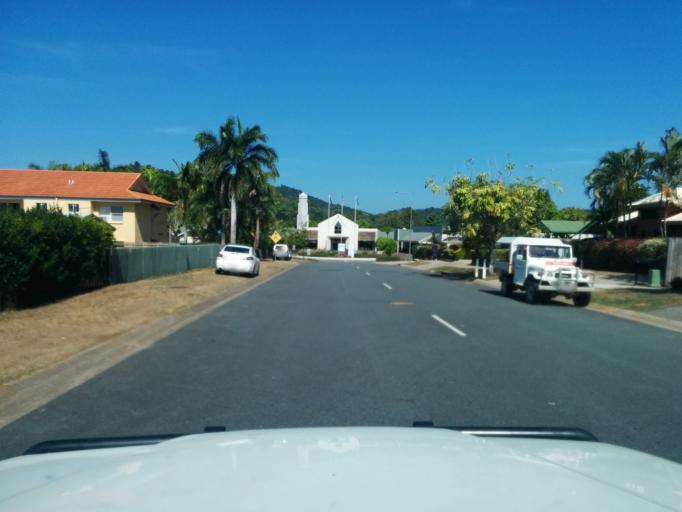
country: AU
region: Queensland
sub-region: Cairns
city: Redlynch
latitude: -16.8891
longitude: 145.6970
